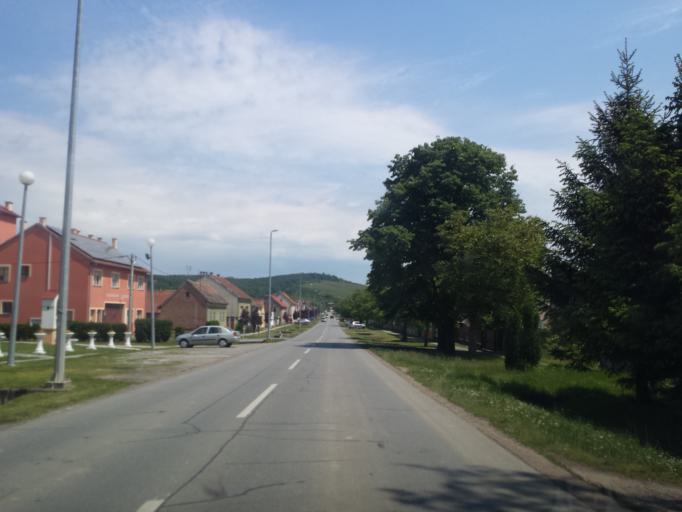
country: HR
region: Brodsko-Posavska
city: Oriovac
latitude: 45.1653
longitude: 17.7942
